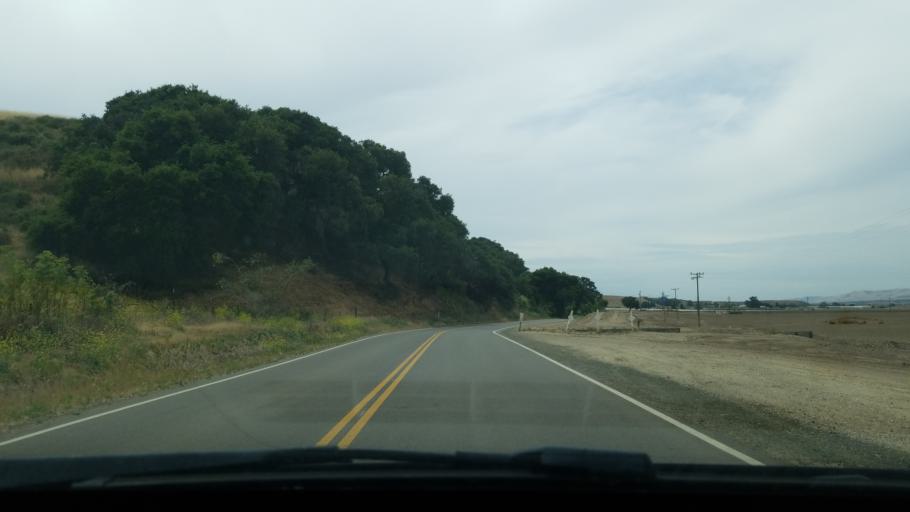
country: US
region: California
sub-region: Santa Barbara County
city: Los Alamos
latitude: 34.8696
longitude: -120.3003
